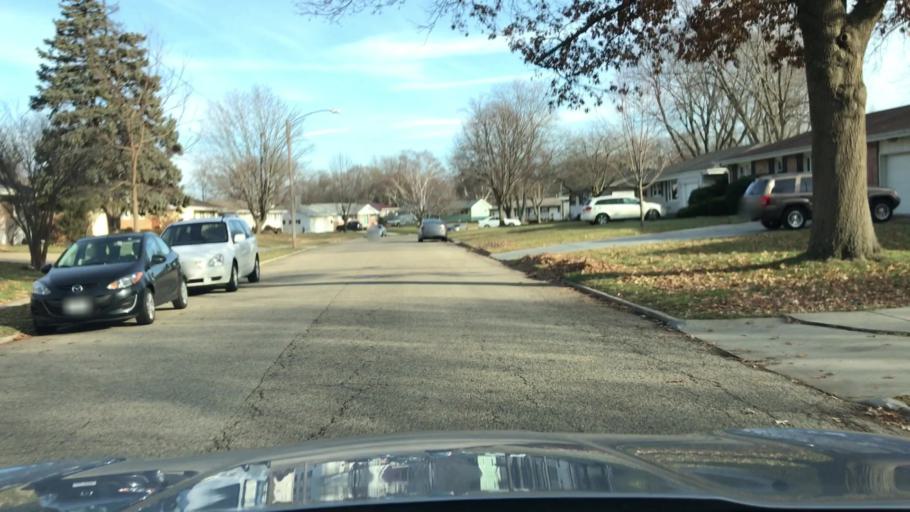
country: US
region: Illinois
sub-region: McLean County
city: Normal
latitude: 40.5022
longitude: -88.9657
